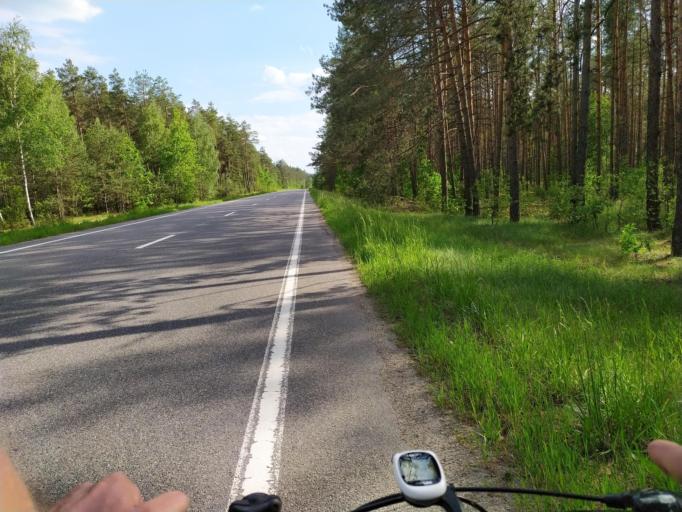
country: BY
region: Brest
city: Zhabinka
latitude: 52.4248
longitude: 24.1227
